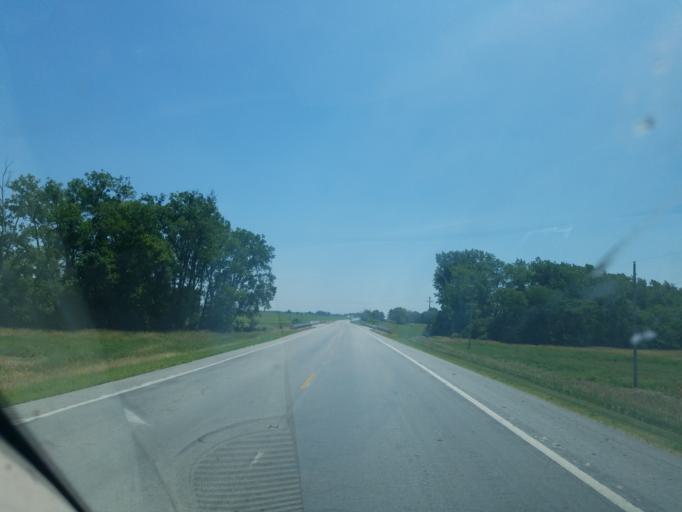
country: US
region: Ohio
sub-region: Mercer County
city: Rockford
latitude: 40.7270
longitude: -84.7394
